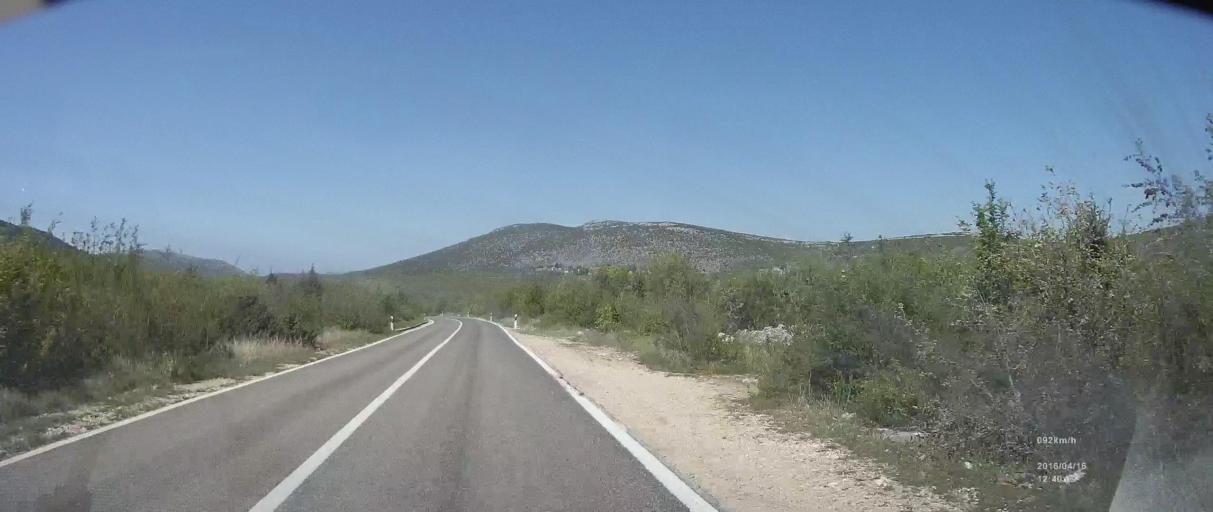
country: HR
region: Sibensko-Kniniska
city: Rogoznica
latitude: 43.6225
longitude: 16.1107
